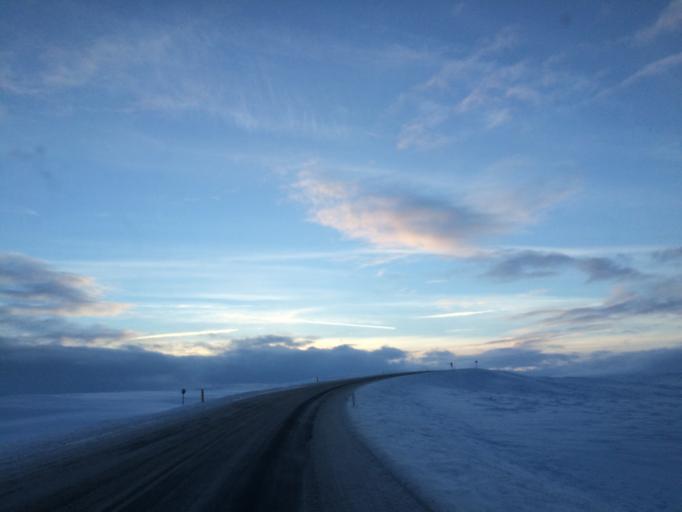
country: IS
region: South
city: Hveragerdi
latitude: 64.2399
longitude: -21.1868
